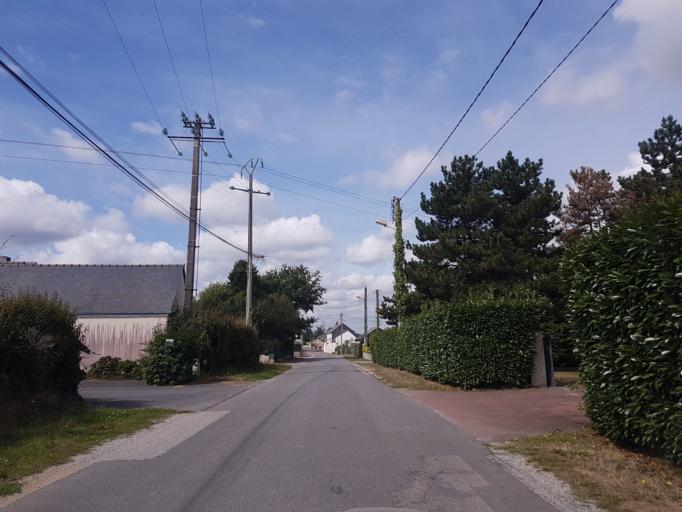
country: FR
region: Pays de la Loire
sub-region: Departement de la Loire-Atlantique
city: Petit-Mars
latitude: 47.3875
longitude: -1.4318
